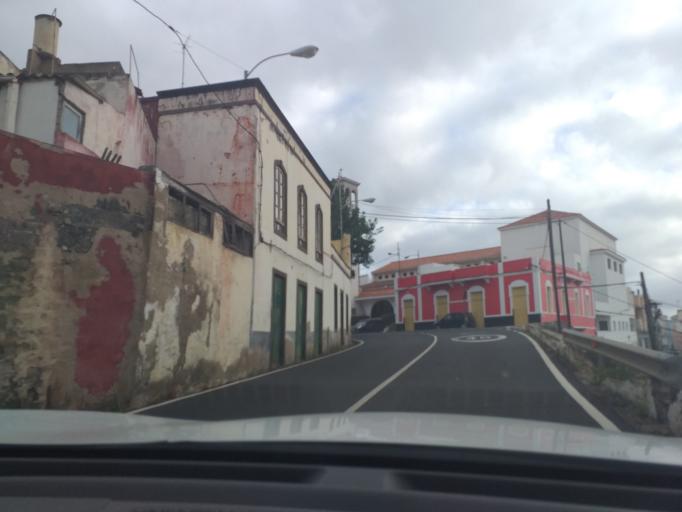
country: ES
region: Canary Islands
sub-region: Provincia de Las Palmas
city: Arucas
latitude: 28.1169
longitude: -15.4918
